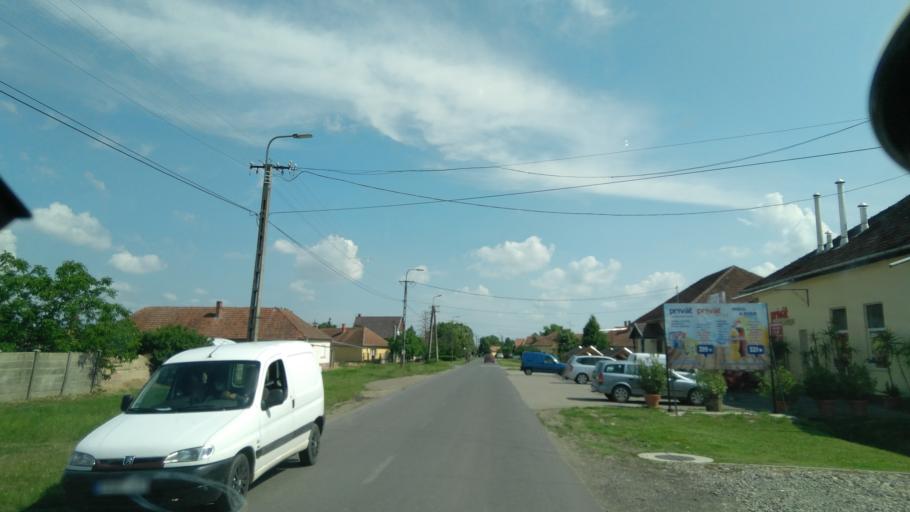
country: HU
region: Bekes
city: Doboz
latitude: 46.7318
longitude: 21.2395
